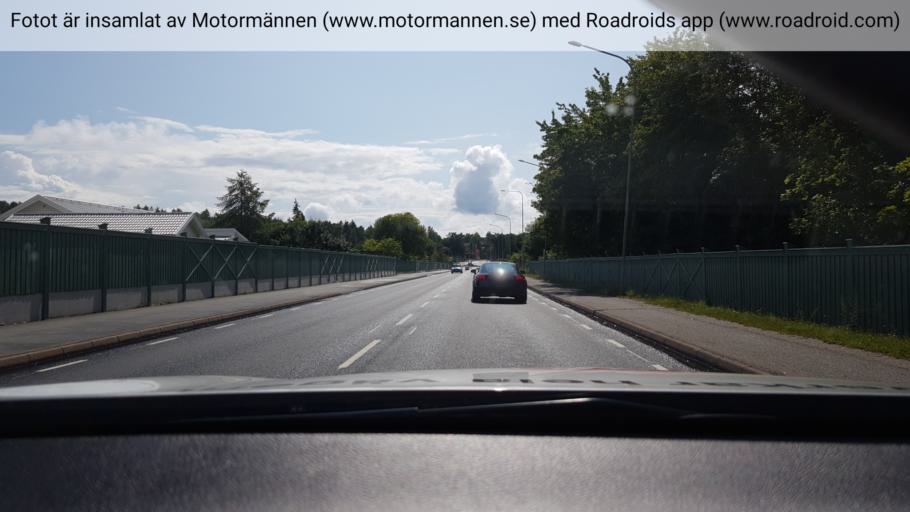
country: SE
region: Stockholm
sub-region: Ekero Kommun
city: Ekeroe
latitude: 59.2834
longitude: 17.7917
